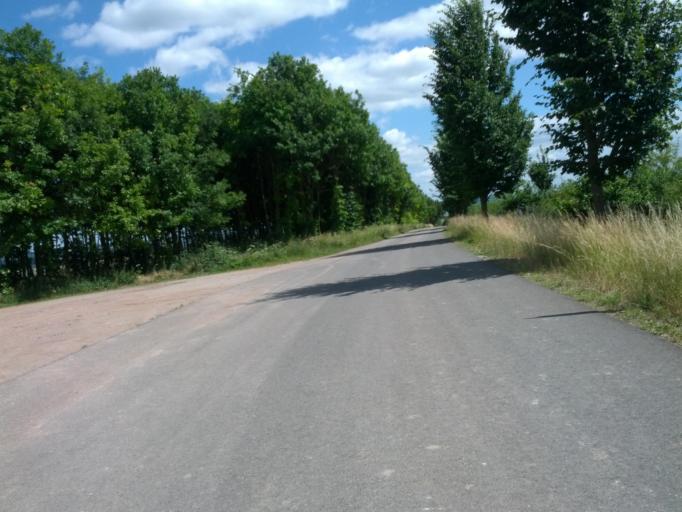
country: DE
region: Thuringia
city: Bischofroda
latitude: 51.0194
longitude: 10.3413
